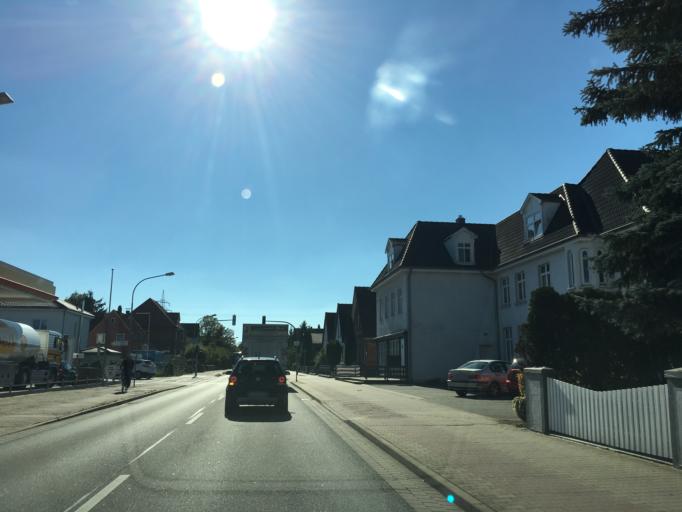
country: DE
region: Lower Saxony
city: Winsen
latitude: 53.3484
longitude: 10.2070
